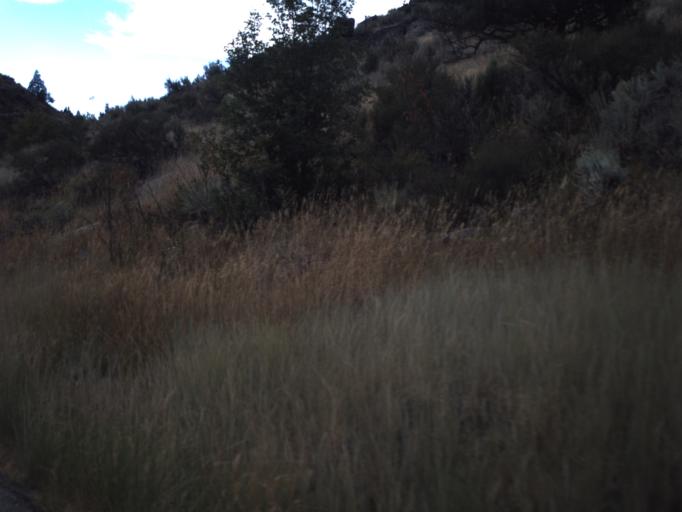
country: US
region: Utah
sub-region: Cache County
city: Millville
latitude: 41.6051
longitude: -111.5983
